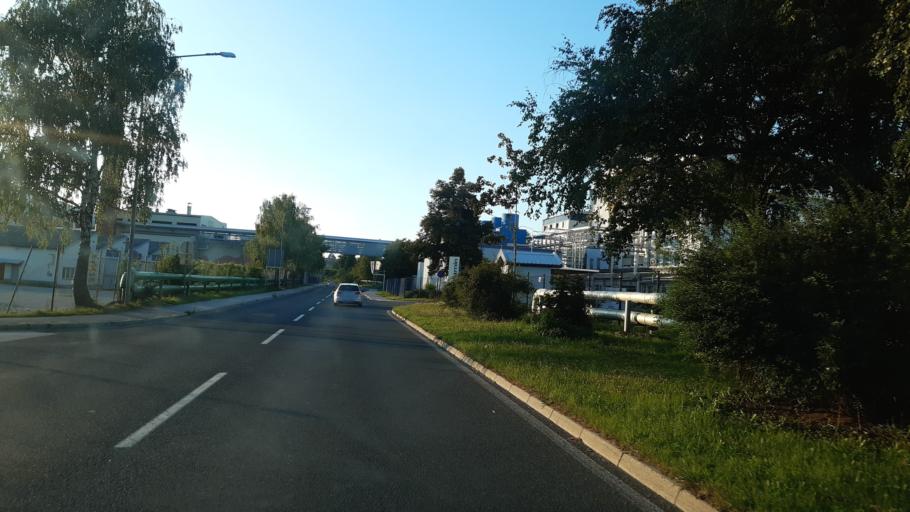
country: SI
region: Kocevje
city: Kocevje
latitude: 45.6408
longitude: 14.8634
